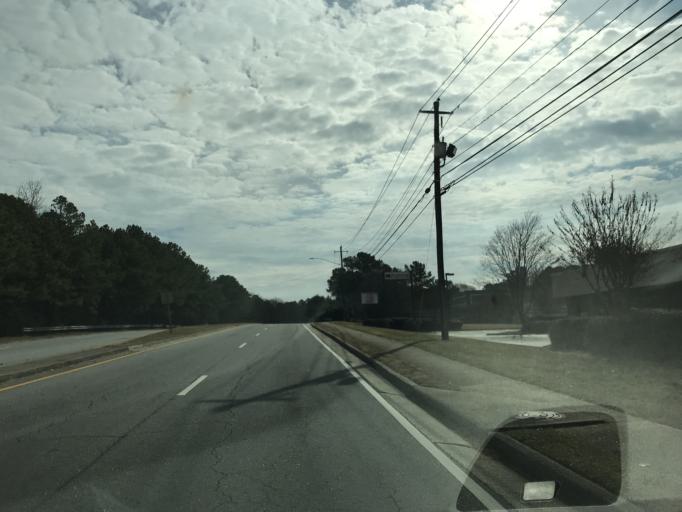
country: US
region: Georgia
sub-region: DeKalb County
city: Tucker
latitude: 33.8426
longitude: -84.2436
